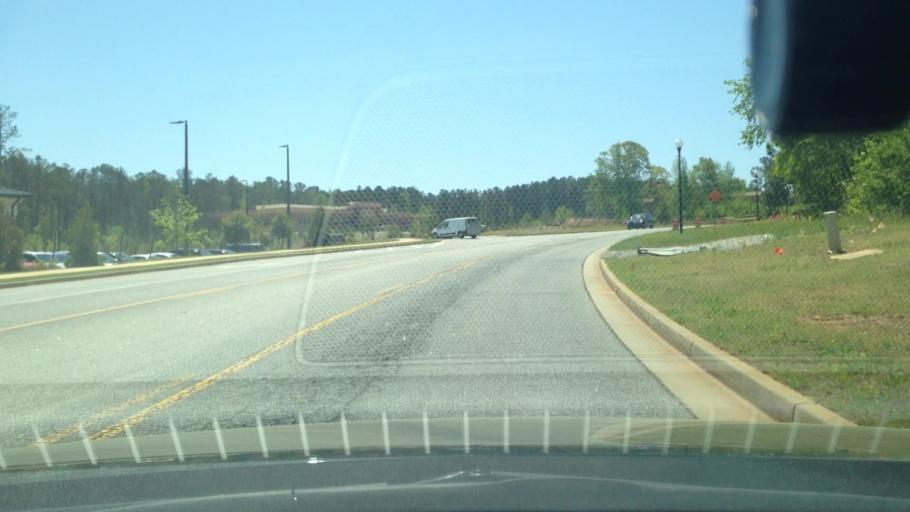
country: US
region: Georgia
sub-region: Coweta County
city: East Newnan
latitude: 33.3630
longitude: -84.7526
